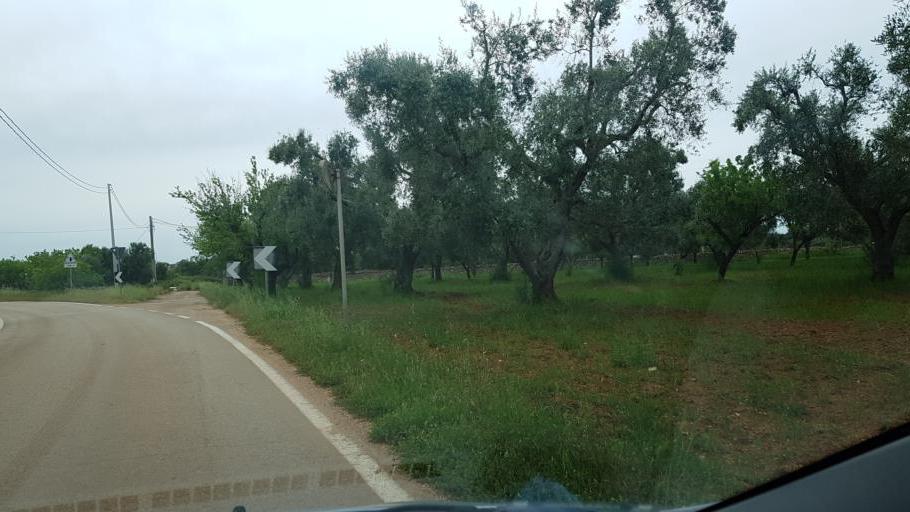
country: IT
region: Apulia
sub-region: Provincia di Brindisi
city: San Vito dei Normanni
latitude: 40.6692
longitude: 17.7575
